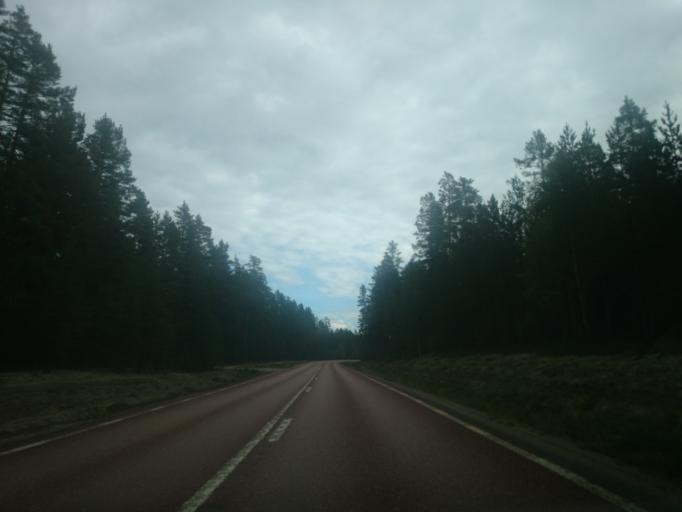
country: SE
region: Gaevleborg
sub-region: Ljusdals Kommun
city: Farila
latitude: 61.9006
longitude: 15.6443
